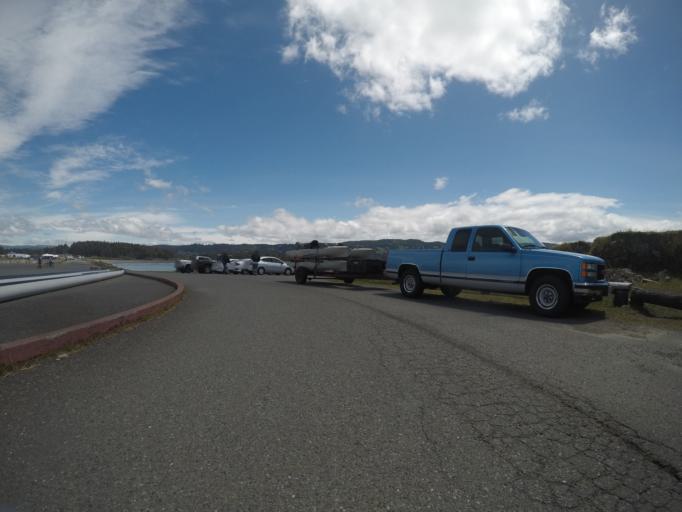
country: US
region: California
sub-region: Del Norte County
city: Crescent City
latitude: 41.7402
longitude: -124.1839
